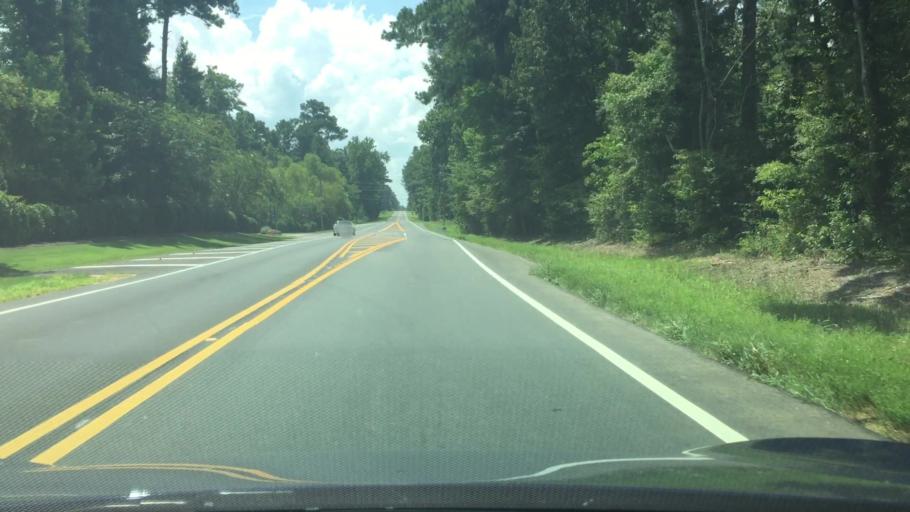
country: US
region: Alabama
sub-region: Montgomery County
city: Pike Road
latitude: 32.3440
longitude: -86.0950
